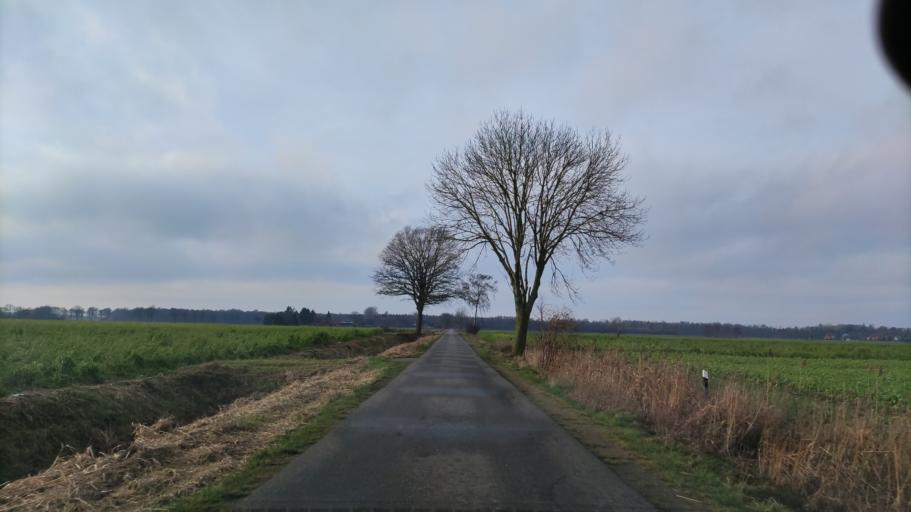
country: DE
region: Lower Saxony
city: Ludersburg
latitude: 53.3066
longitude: 10.5836
